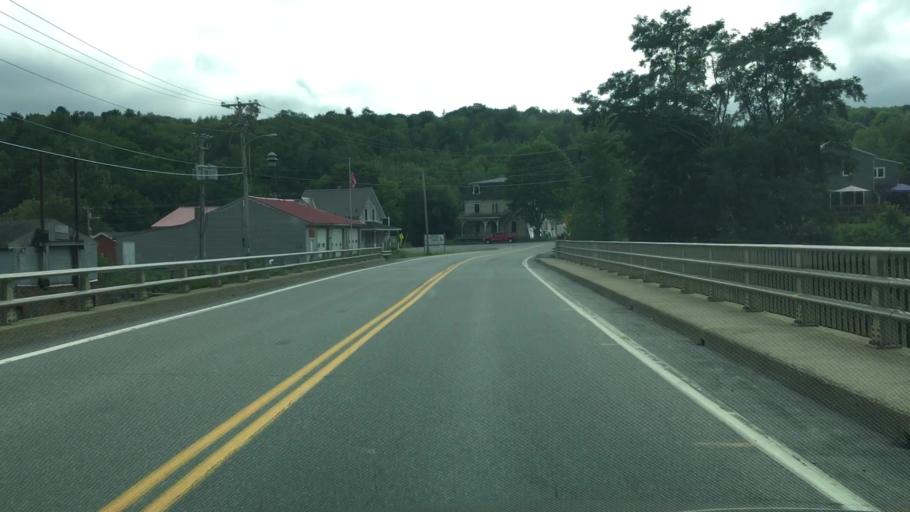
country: US
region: Maine
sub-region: Waldo County
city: Frankfort
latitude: 44.6095
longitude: -68.8733
